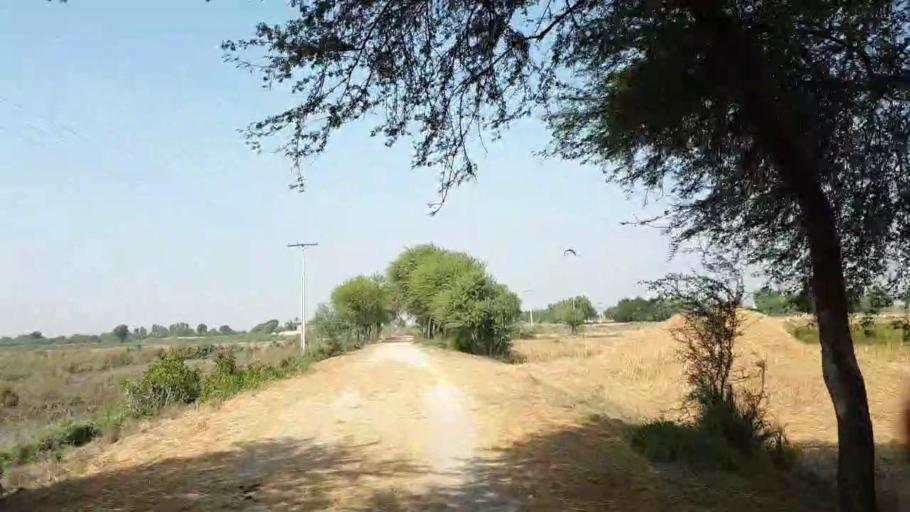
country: PK
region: Sindh
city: Tando Muhammad Khan
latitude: 25.0318
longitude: 68.4048
